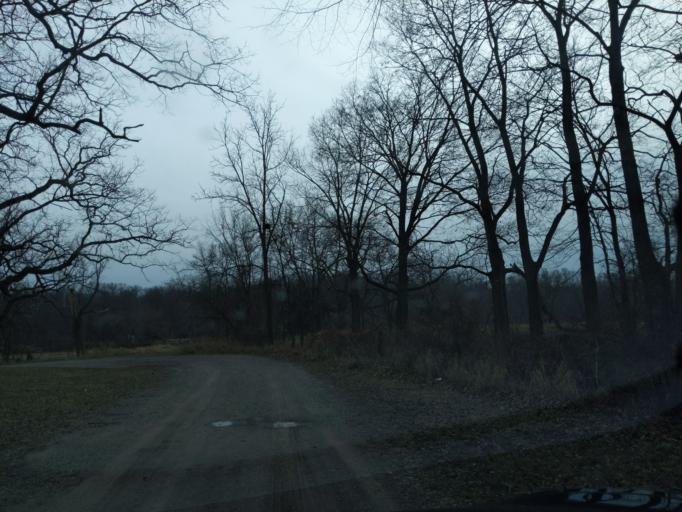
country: US
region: Michigan
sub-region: Ionia County
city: Portland
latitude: 42.9780
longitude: -84.9420
